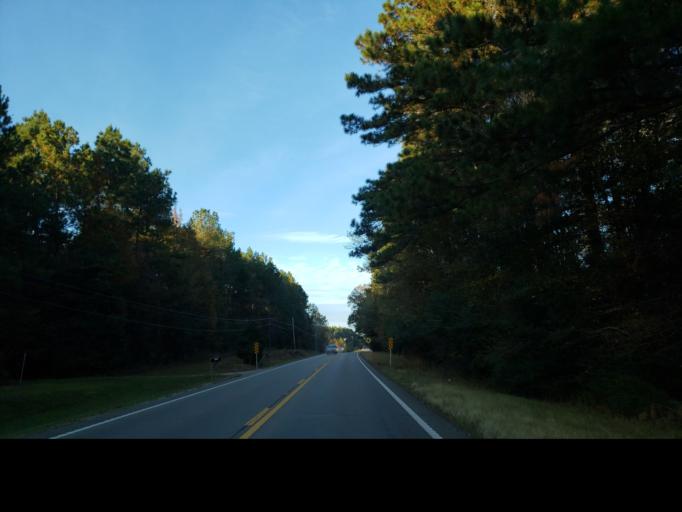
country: US
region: Mississippi
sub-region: Lamar County
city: Purvis
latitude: 31.1648
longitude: -89.3934
